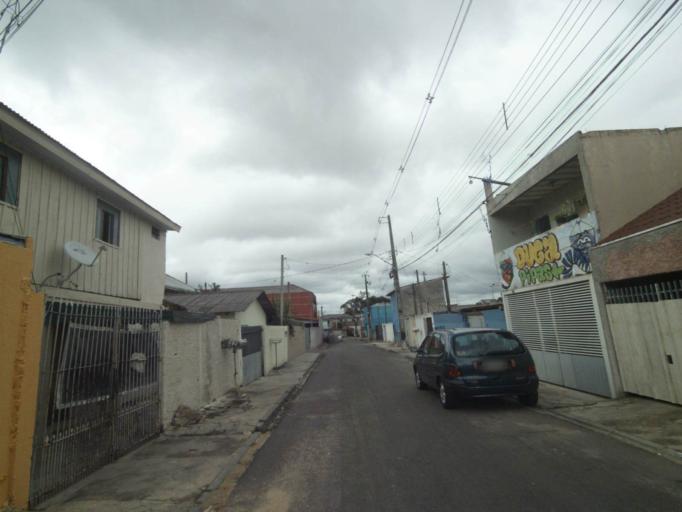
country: BR
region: Parana
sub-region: Curitiba
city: Curitiba
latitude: -25.4847
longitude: -49.3063
